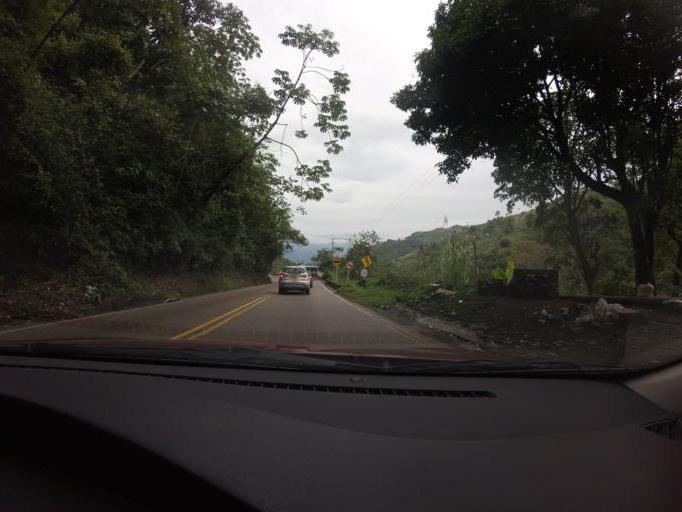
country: CO
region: Cundinamarca
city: Villeta
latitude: 5.0252
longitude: -74.5258
